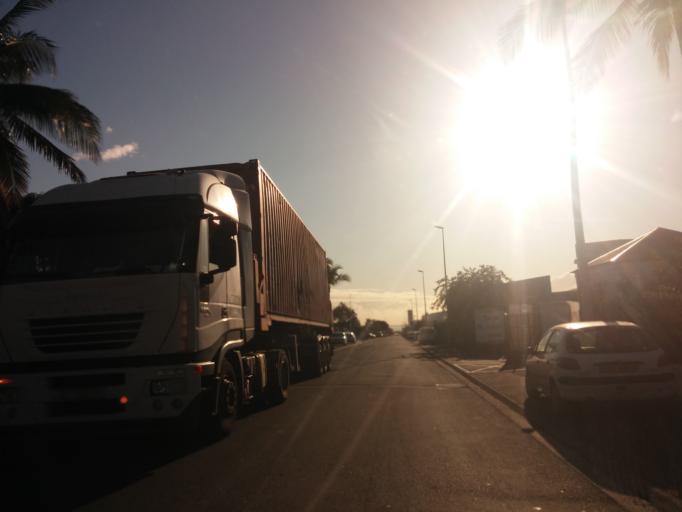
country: RE
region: Reunion
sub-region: Reunion
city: Le Port
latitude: -20.9390
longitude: 55.3142
